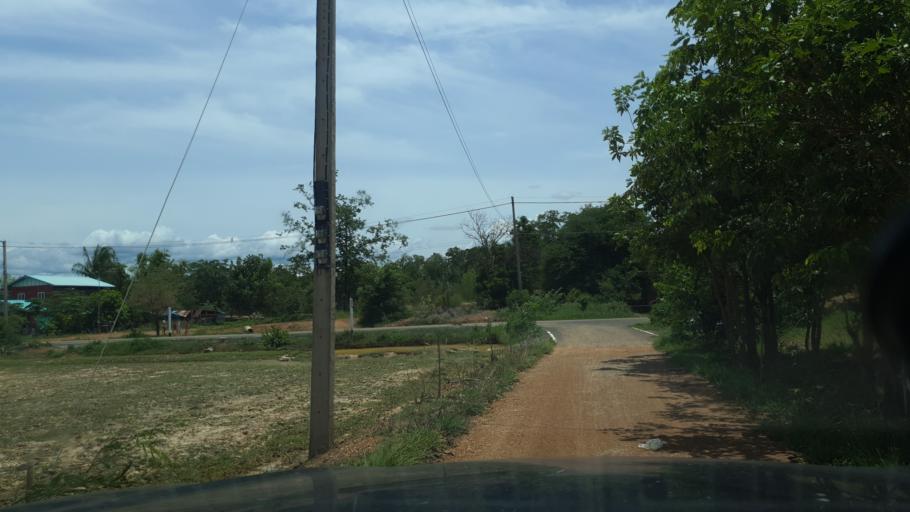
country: TH
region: Sukhothai
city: Ban Na
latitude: 17.1505
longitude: 99.6686
